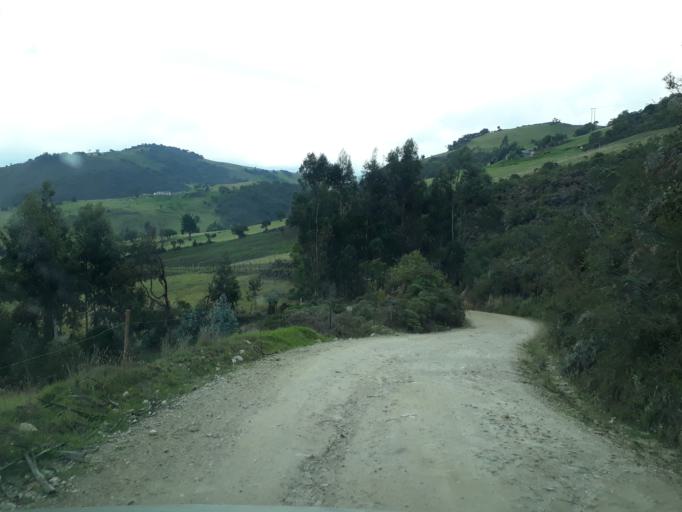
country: CO
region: Cundinamarca
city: Lenguazaque
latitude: 5.2591
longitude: -73.6894
